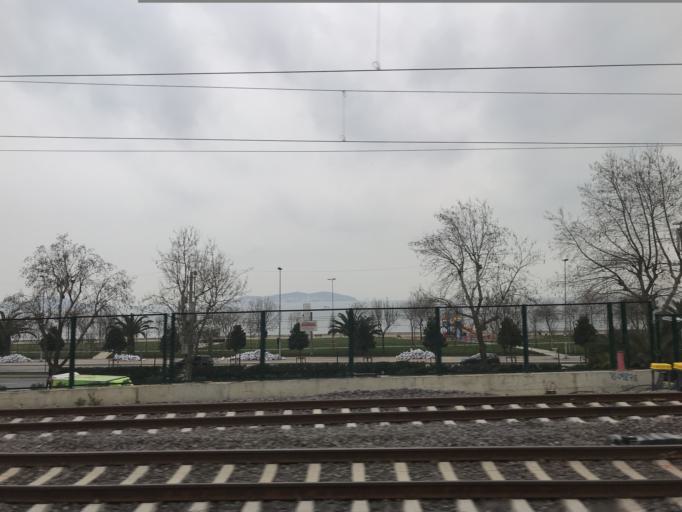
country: TR
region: Istanbul
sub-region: Atasehir
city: Atasehir
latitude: 40.9479
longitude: 29.1015
